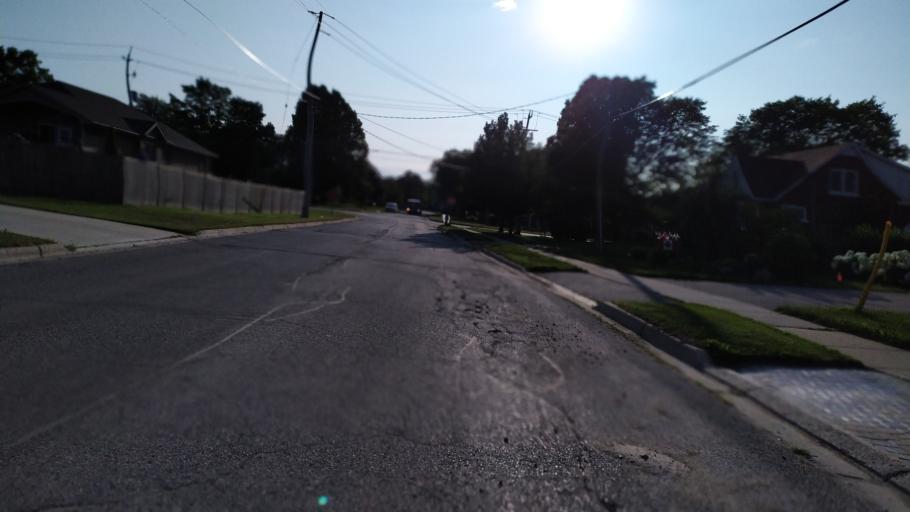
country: CA
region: Ontario
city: Stratford
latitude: 43.3726
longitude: -80.9571
